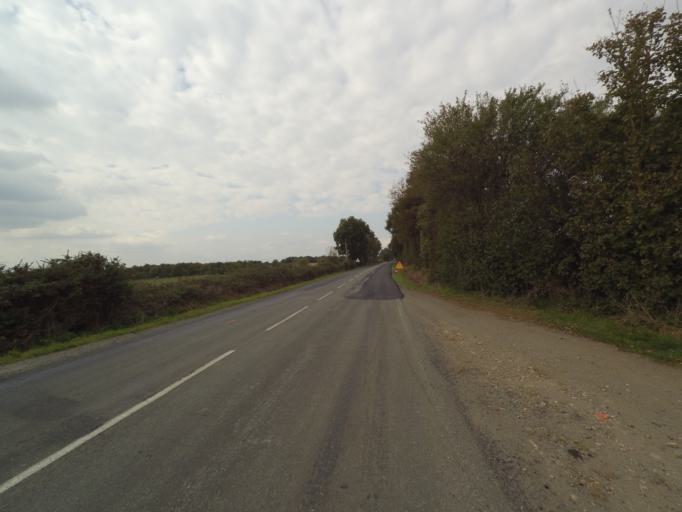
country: FR
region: Pays de la Loire
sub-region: Departement de la Vendee
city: Bouffere
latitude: 46.9851
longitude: -1.3557
